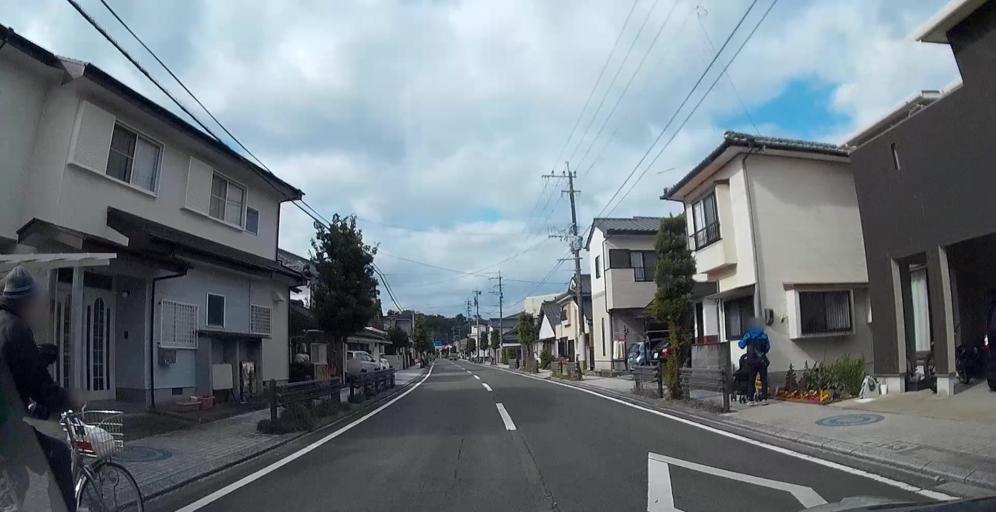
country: JP
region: Kumamoto
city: Minamata
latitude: 32.2118
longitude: 130.3907
